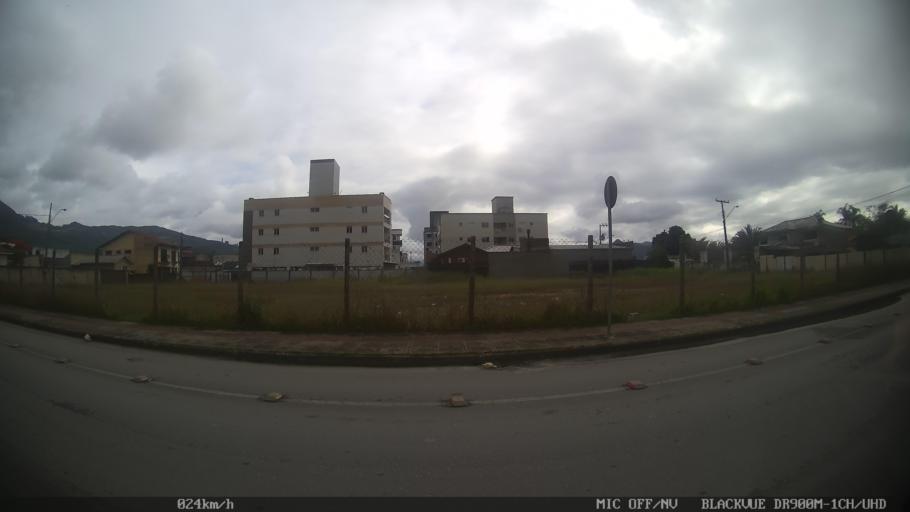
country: BR
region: Santa Catarina
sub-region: Biguacu
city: Biguacu
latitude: -27.5139
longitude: -48.6439
